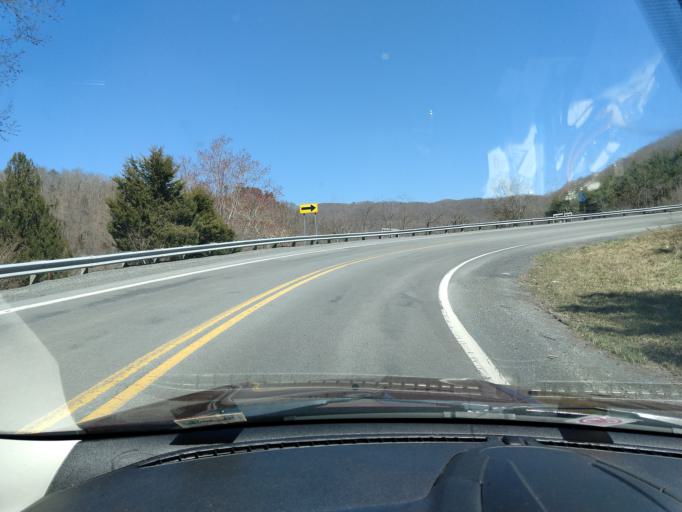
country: US
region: West Virginia
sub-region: Summers County
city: Hinton
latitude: 37.7668
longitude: -80.8896
